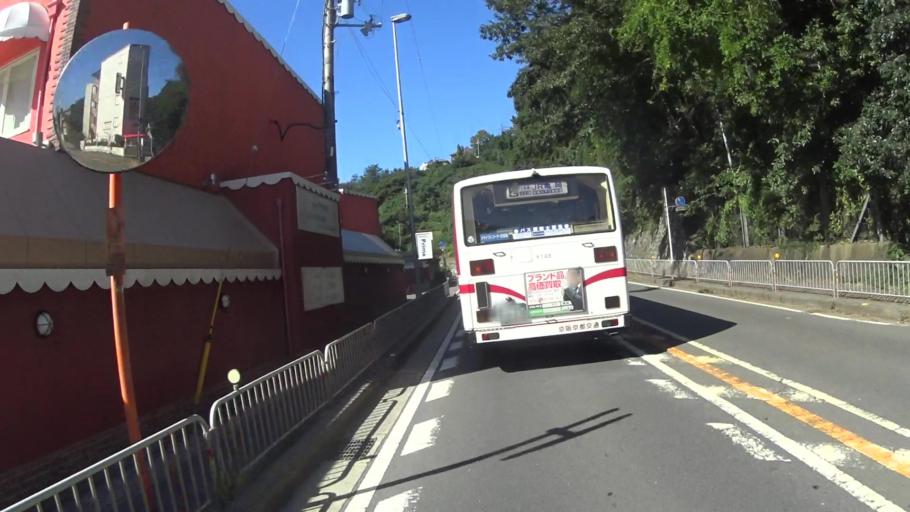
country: JP
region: Kyoto
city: Muko
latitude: 34.9788
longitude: 135.6522
